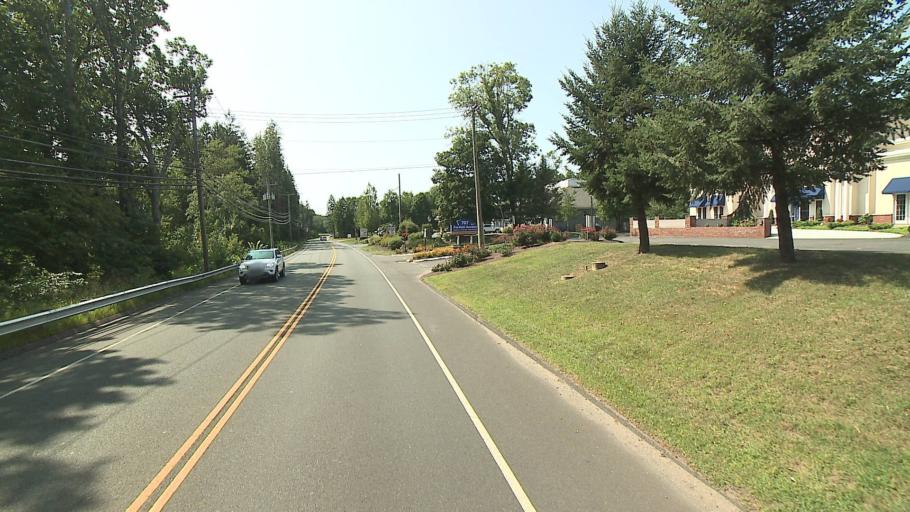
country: US
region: Connecticut
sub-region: Fairfield County
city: Newtown
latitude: 41.3401
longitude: -73.2624
